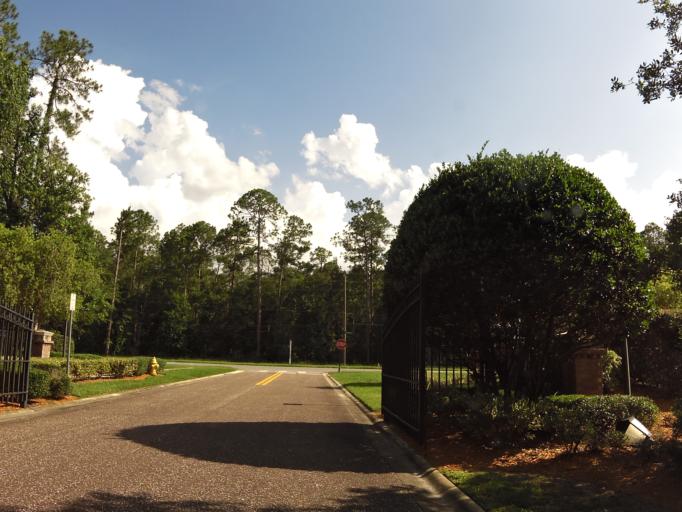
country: US
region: Florida
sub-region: Saint Johns County
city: Fruit Cove
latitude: 30.0629
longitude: -81.6508
